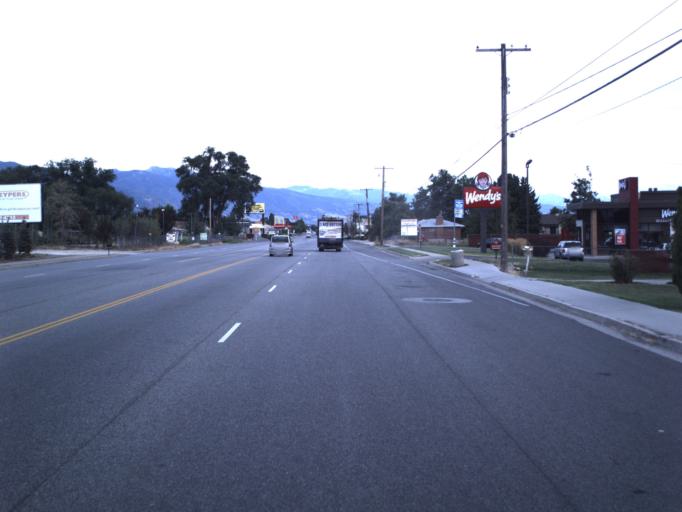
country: US
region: Utah
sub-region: Davis County
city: Clearfield
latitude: 41.0946
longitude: -112.0066
